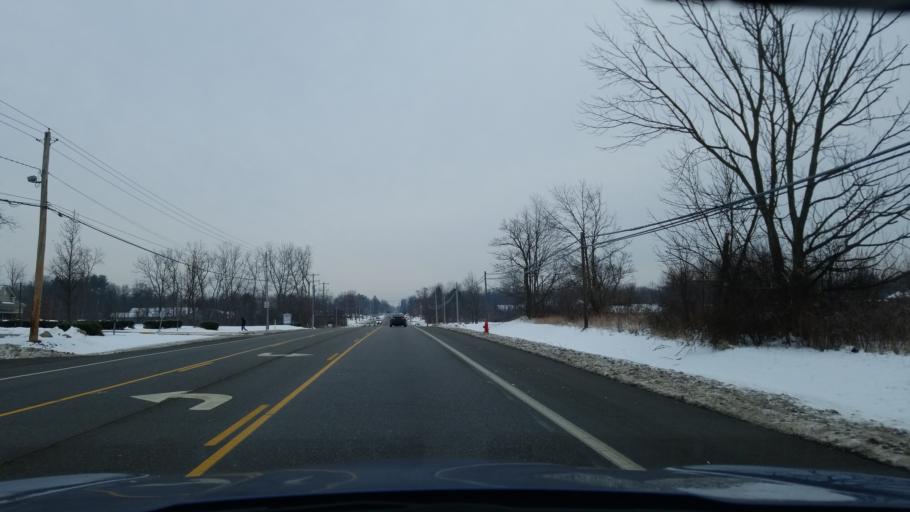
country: US
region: Ohio
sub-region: Summit County
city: Northfield
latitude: 41.3143
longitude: -81.5554
